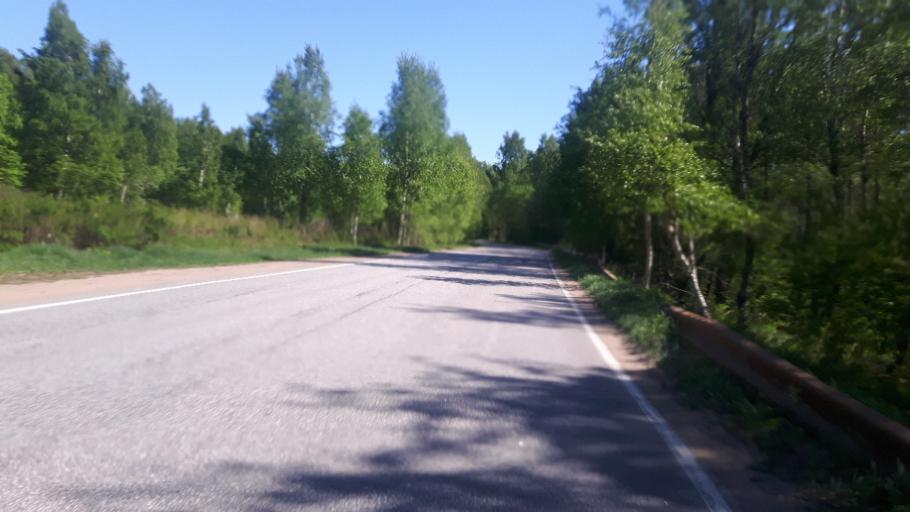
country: RU
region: Leningrad
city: Glebychevo
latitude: 60.2815
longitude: 28.8824
